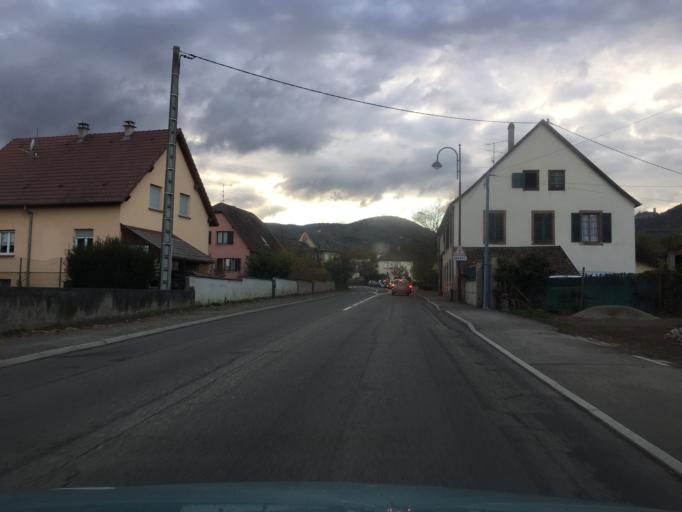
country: FR
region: Alsace
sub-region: Departement du Haut-Rhin
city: Ribeauville
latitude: 48.1923
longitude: 7.3320
